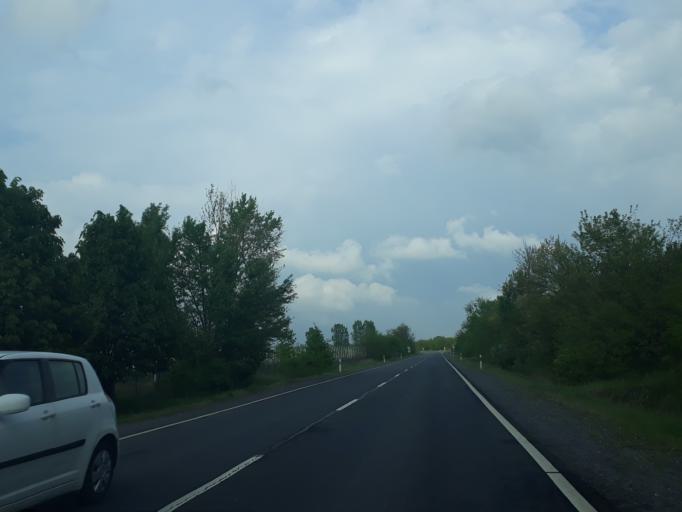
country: HU
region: Szabolcs-Szatmar-Bereg
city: Nyirtass
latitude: 48.1184
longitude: 21.9980
